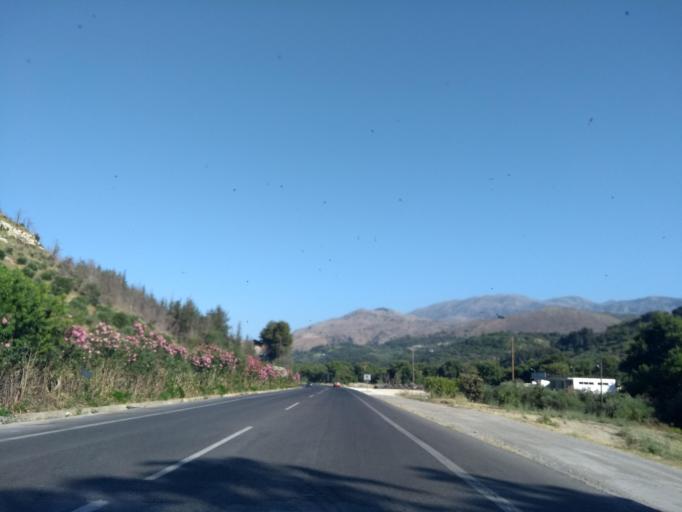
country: GR
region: Crete
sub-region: Nomos Chanias
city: Georgioupolis
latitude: 35.3746
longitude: 24.2095
